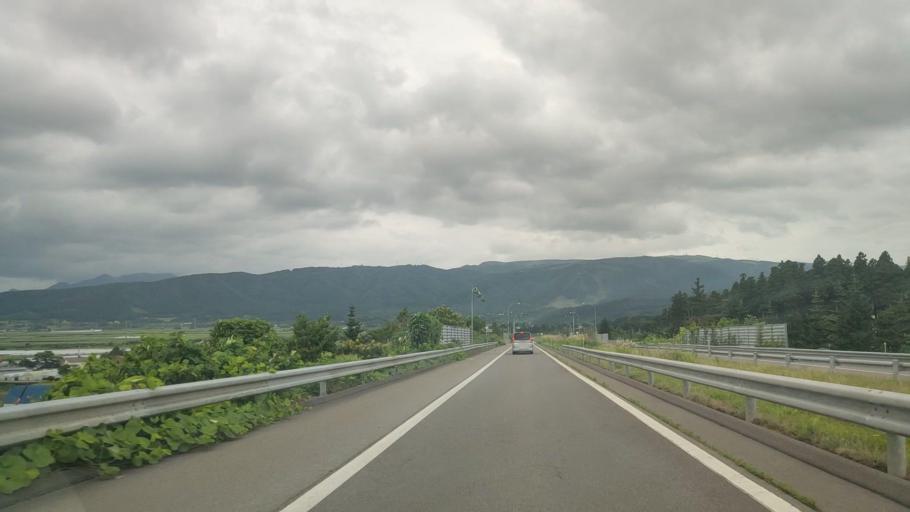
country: JP
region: Hokkaido
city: Nanae
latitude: 41.9211
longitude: 140.6767
